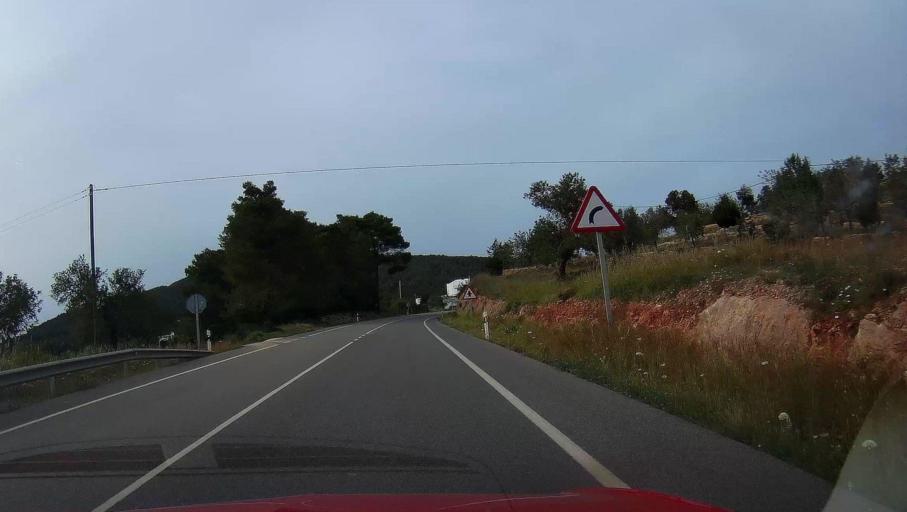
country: ES
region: Balearic Islands
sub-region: Illes Balears
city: Sant Joan de Labritja
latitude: 39.0644
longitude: 1.4945
